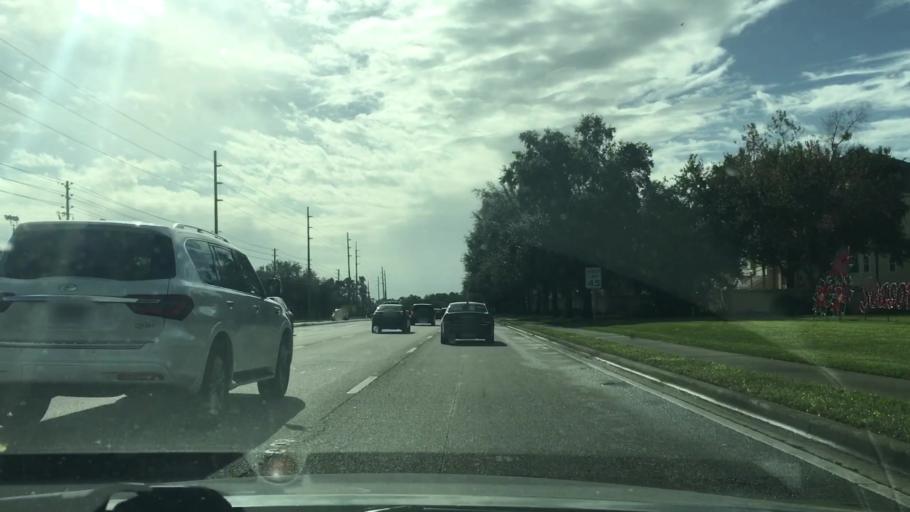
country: US
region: Florida
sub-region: Osceola County
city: Celebration
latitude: 28.3680
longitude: -81.5029
